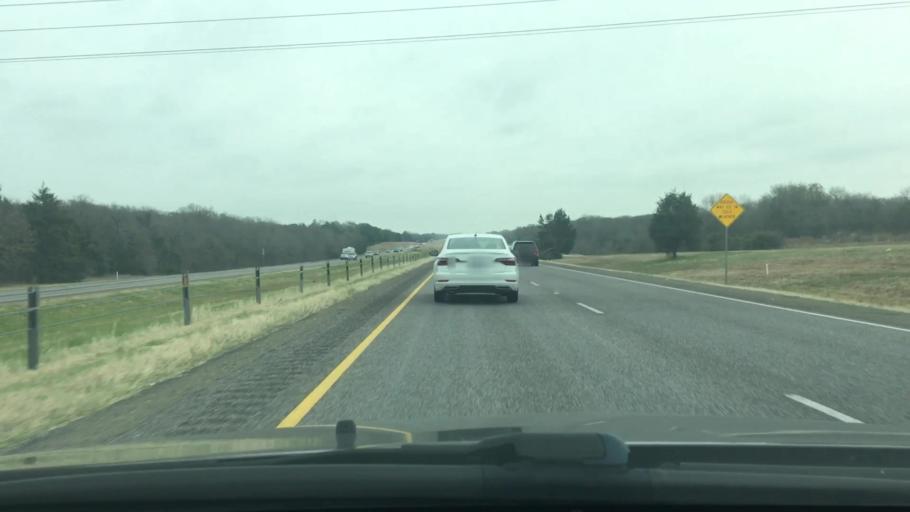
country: US
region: Texas
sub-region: Freestone County
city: Fairfield
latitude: 31.7527
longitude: -96.2022
